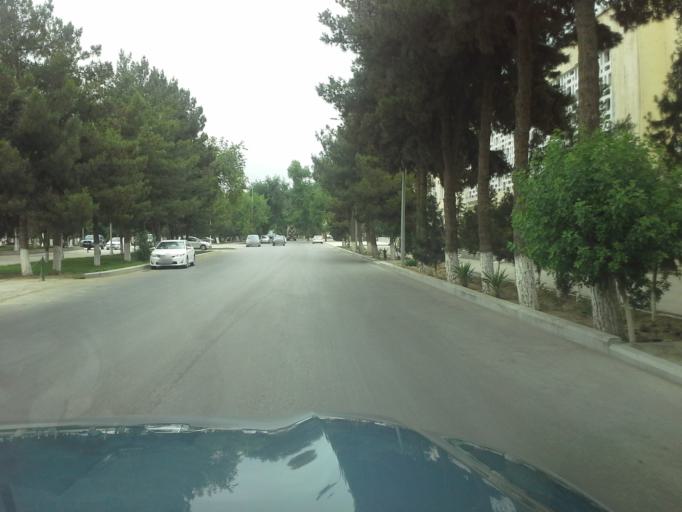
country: TM
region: Ahal
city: Ashgabat
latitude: 37.9551
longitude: 58.3658
